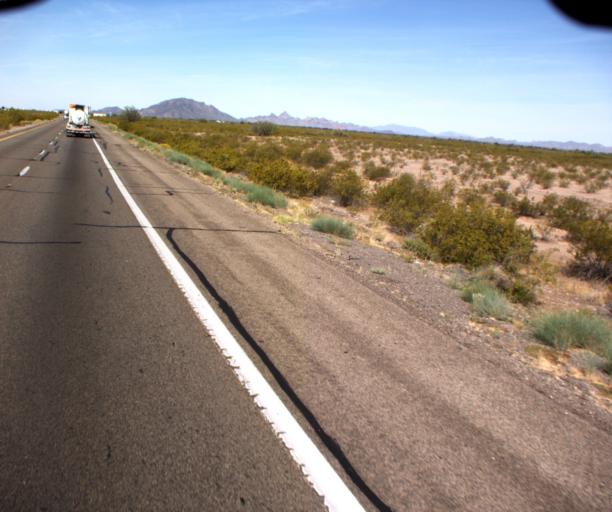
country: US
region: Arizona
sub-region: Maricopa County
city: Buckeye
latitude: 33.4999
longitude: -112.9475
